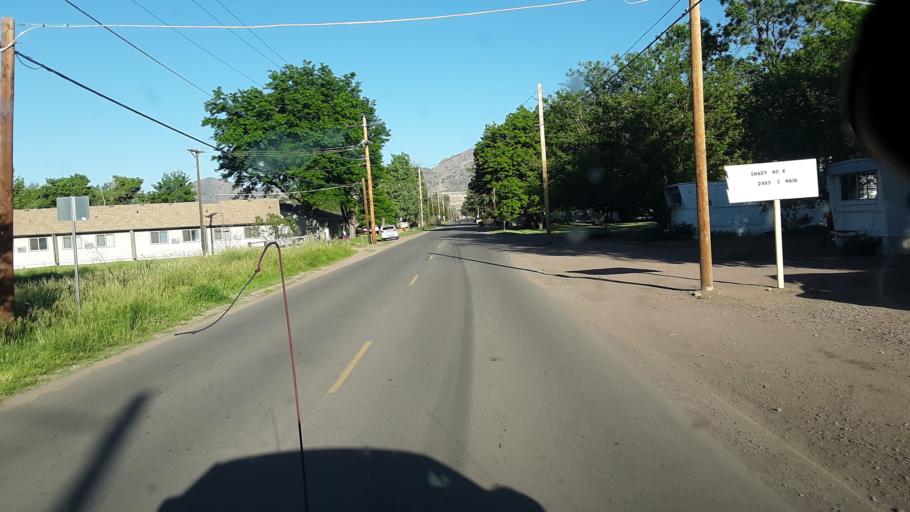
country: US
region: Colorado
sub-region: Fremont County
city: Lincoln Park
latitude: 38.4467
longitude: -105.2112
